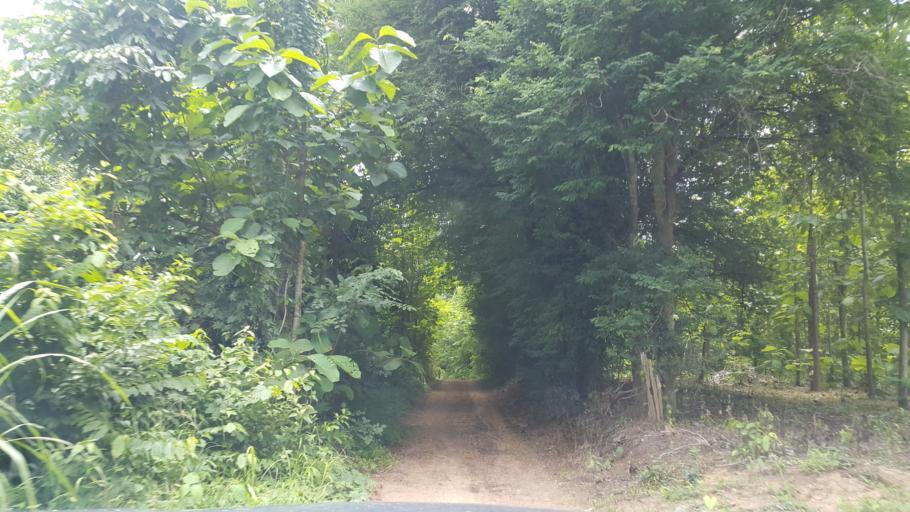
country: TH
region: Sukhothai
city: Thung Saliam
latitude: 17.3312
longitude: 99.4771
